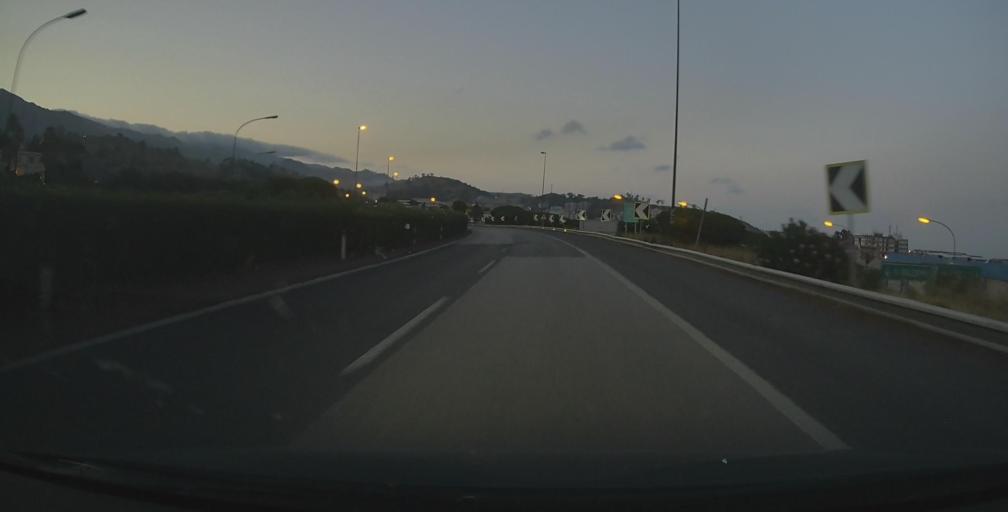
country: IT
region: Sicily
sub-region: Messina
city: Larderia
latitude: 38.1359
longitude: 15.5202
